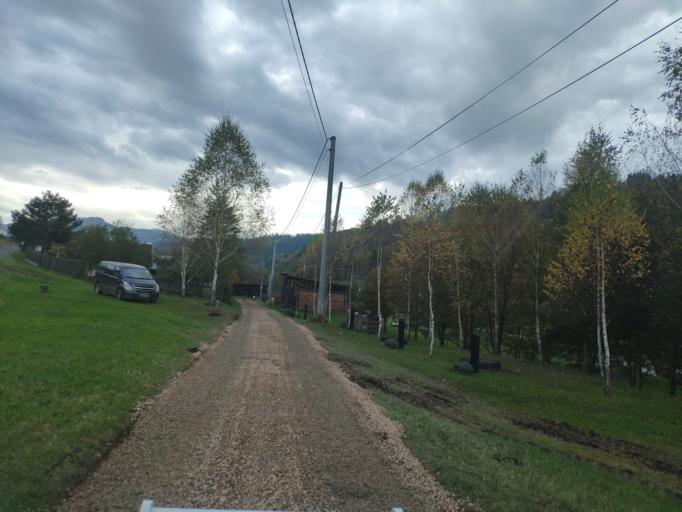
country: SK
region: Kosicky
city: Spisska Nova Ves
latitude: 48.8334
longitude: 20.6375
